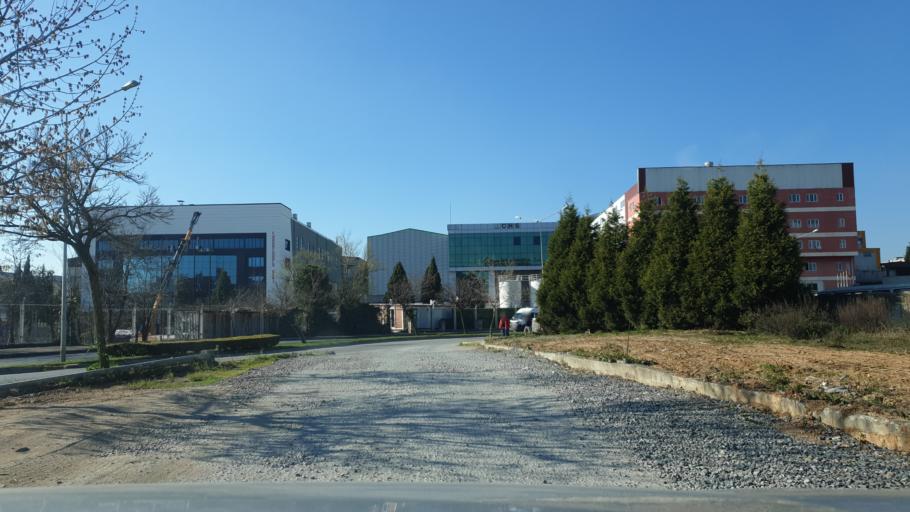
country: TR
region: Kocaeli
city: Balcik
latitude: 40.8778
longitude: 29.3716
